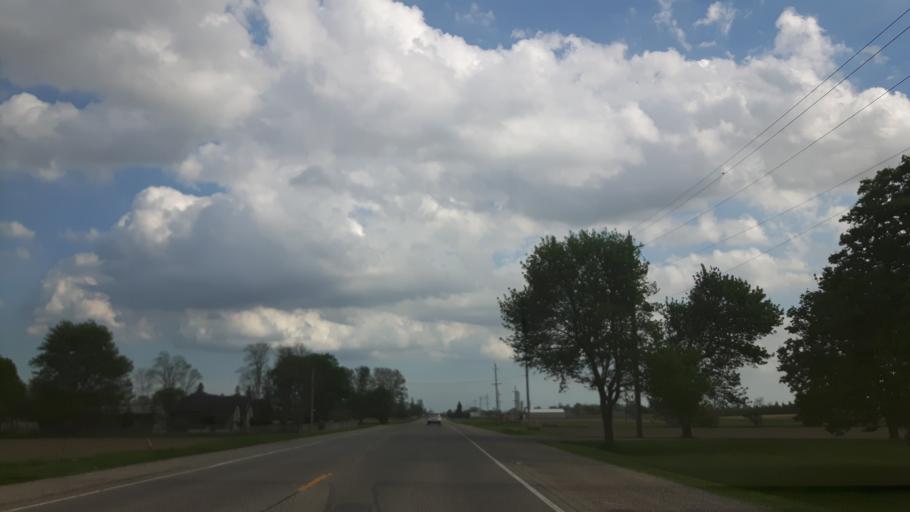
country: CA
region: Ontario
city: South Huron
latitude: 43.3016
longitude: -81.4715
